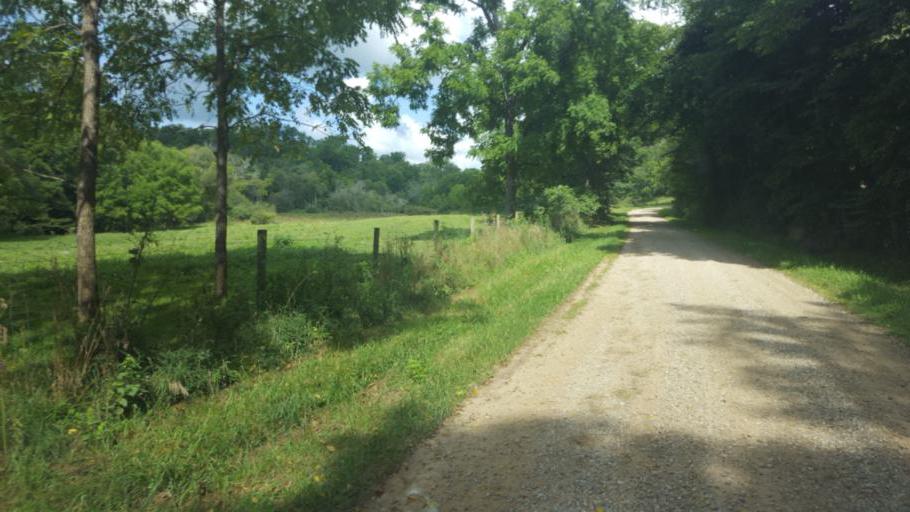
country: US
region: Ohio
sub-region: Knox County
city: Fredericktown
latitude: 40.4822
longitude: -82.6560
